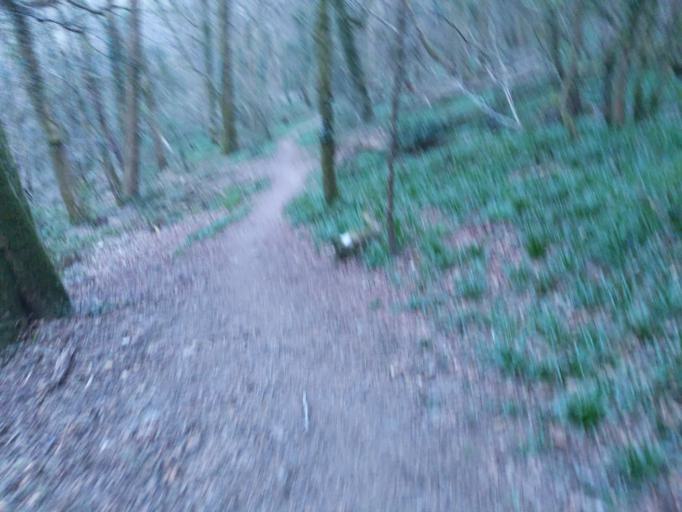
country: GB
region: England
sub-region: Plymouth
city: Plymouth
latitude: 50.4198
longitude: -4.1423
